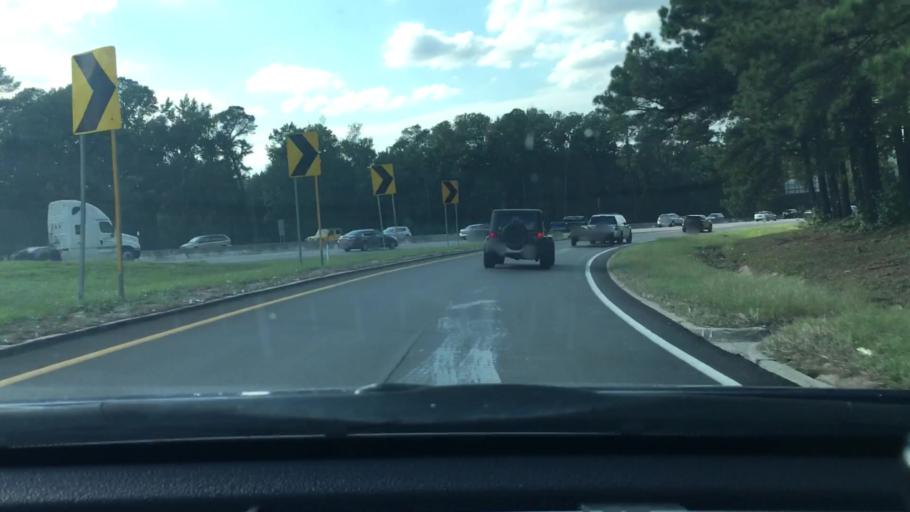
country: US
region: South Carolina
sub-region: Lexington County
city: Saint Andrews
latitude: 34.0391
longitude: -81.1119
